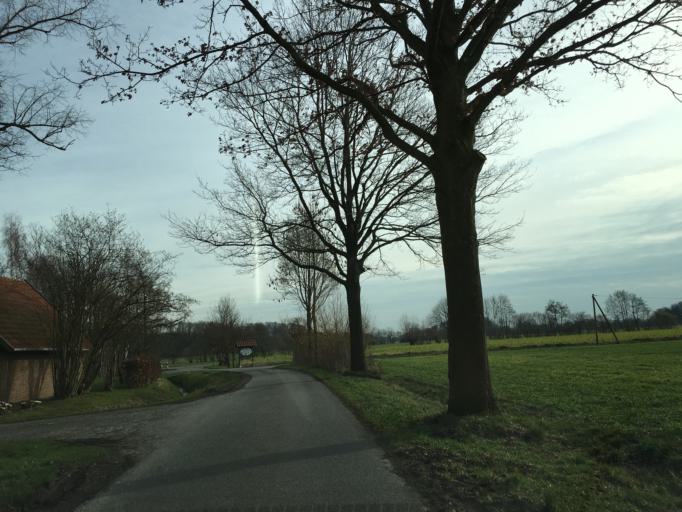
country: DE
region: North Rhine-Westphalia
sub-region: Regierungsbezirk Munster
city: Greven
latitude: 52.0255
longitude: 7.5818
